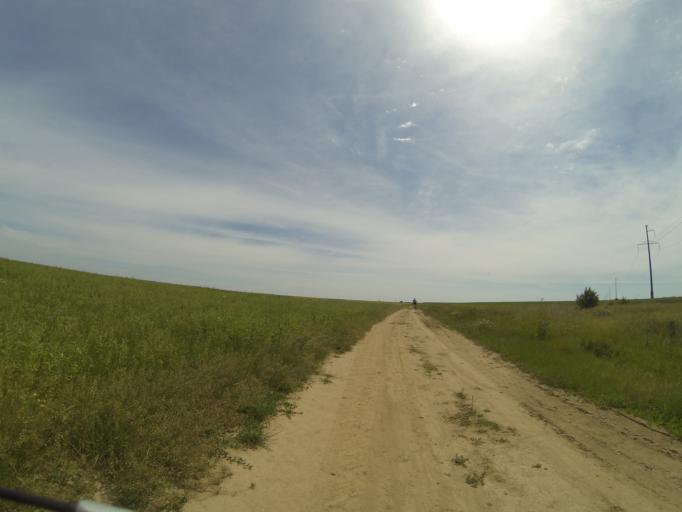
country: RO
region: Dolj
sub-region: Comuna Ghindeni
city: Ghindeni
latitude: 44.2072
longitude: 23.9483
